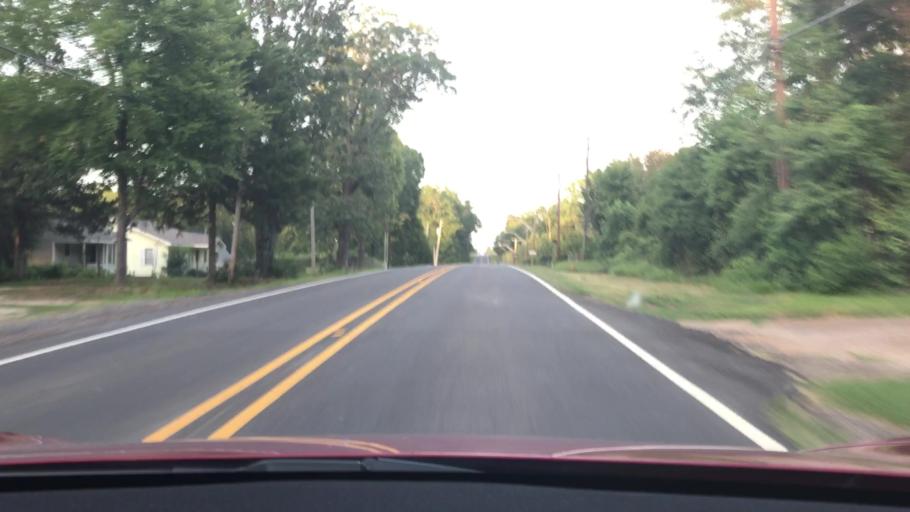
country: US
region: Louisiana
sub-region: De Soto Parish
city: Stonewall
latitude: 32.3910
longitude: -93.7599
